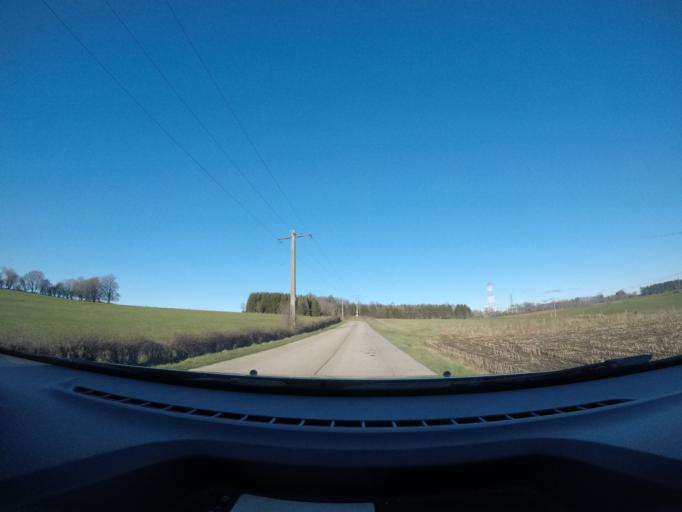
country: BE
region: Wallonia
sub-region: Province du Luxembourg
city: Bertrix
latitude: 49.8433
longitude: 5.2993
